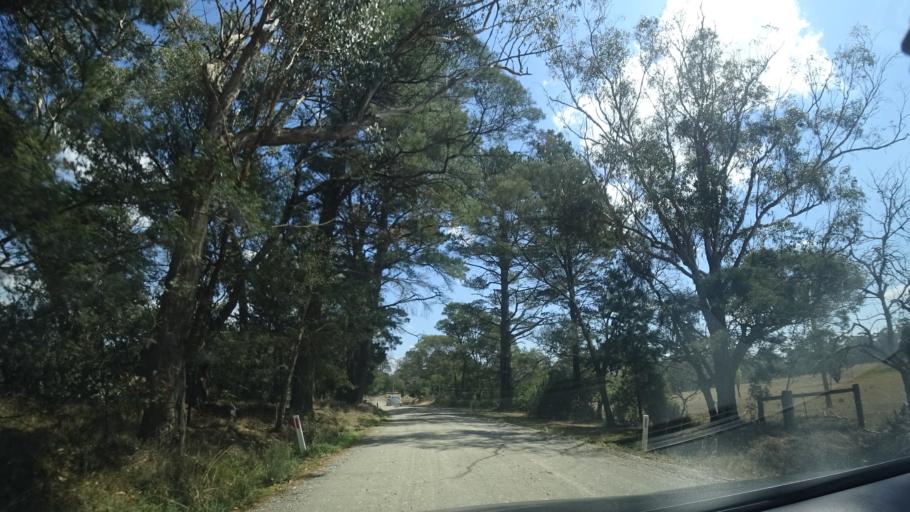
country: AU
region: New South Wales
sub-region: Wingecarribee
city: Bundanoon
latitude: -34.6277
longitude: 150.2604
